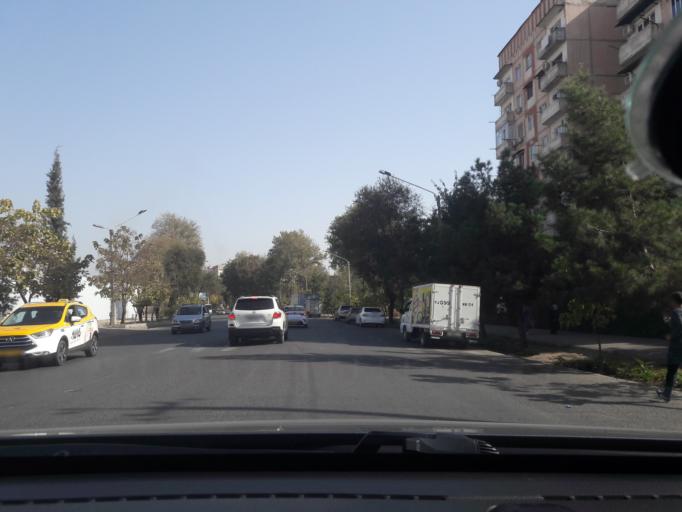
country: TJ
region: Dushanbe
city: Dushanbe
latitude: 38.5183
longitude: 68.7514
